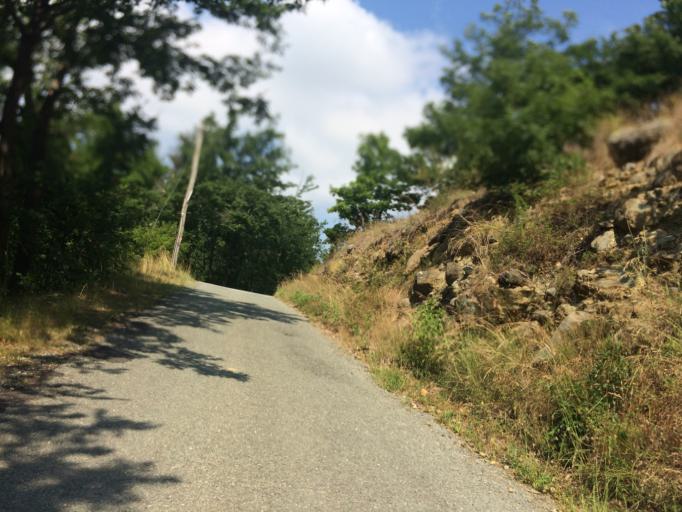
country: IT
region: Liguria
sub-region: Provincia di Savona
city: Molino-Pera
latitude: 44.4856
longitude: 8.3518
